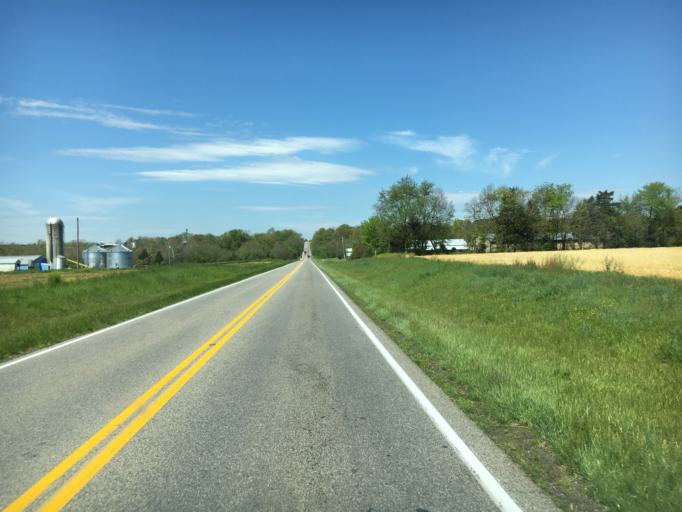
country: US
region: Virginia
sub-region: Rockingham County
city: Grottoes
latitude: 38.2669
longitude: -78.8596
